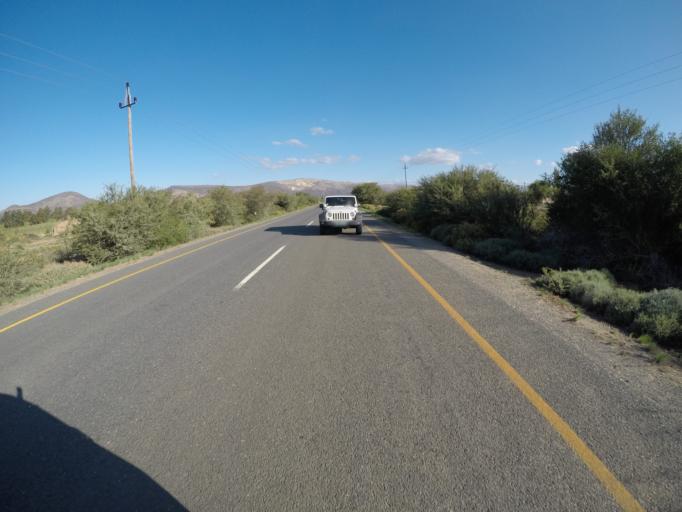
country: ZA
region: Western Cape
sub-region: Cape Winelands District Municipality
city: Ashton
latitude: -33.8020
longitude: 19.7816
